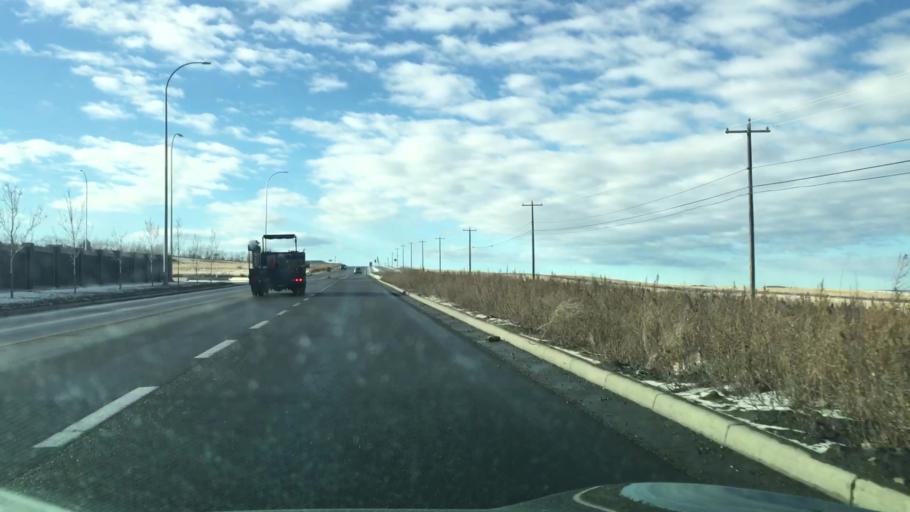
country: CA
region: Alberta
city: Calgary
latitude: 51.1831
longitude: -114.1745
